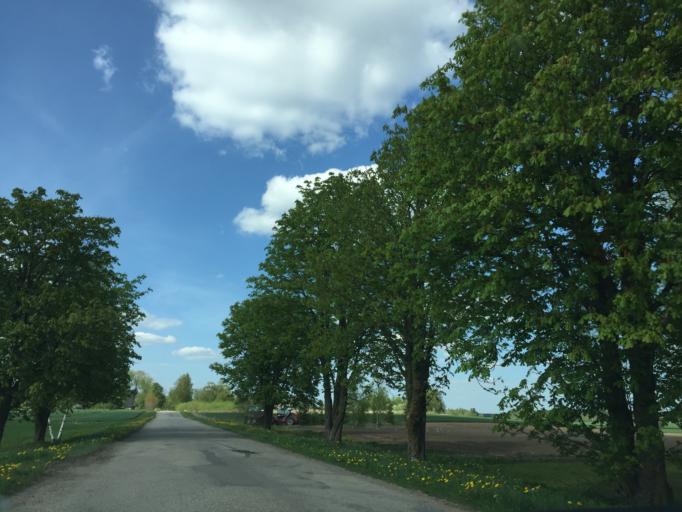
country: LV
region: Vecumnieki
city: Vecumnieki
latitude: 56.4359
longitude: 24.4087
